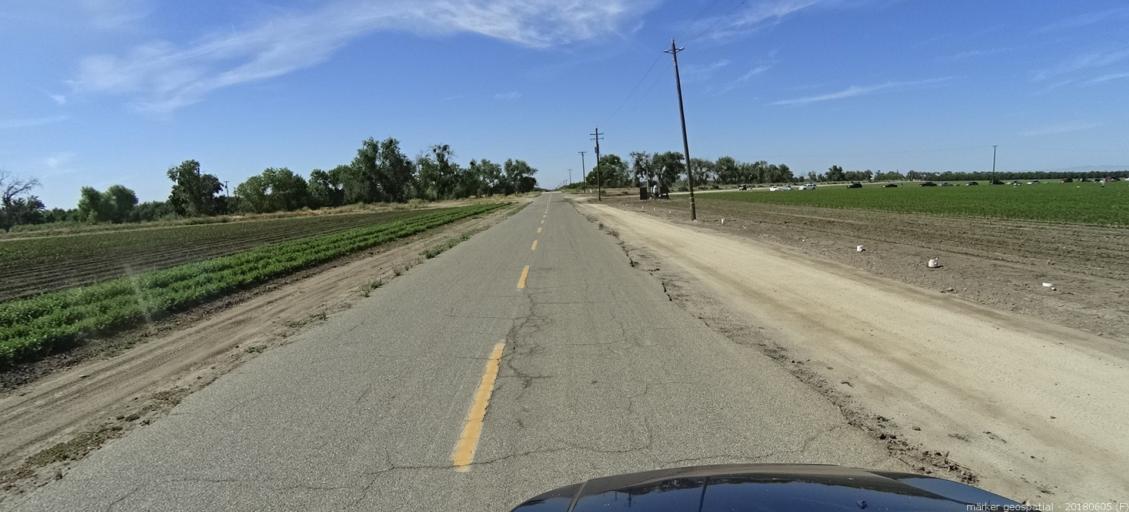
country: US
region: California
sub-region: Madera County
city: Chowchilla
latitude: 37.0667
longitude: -120.4010
